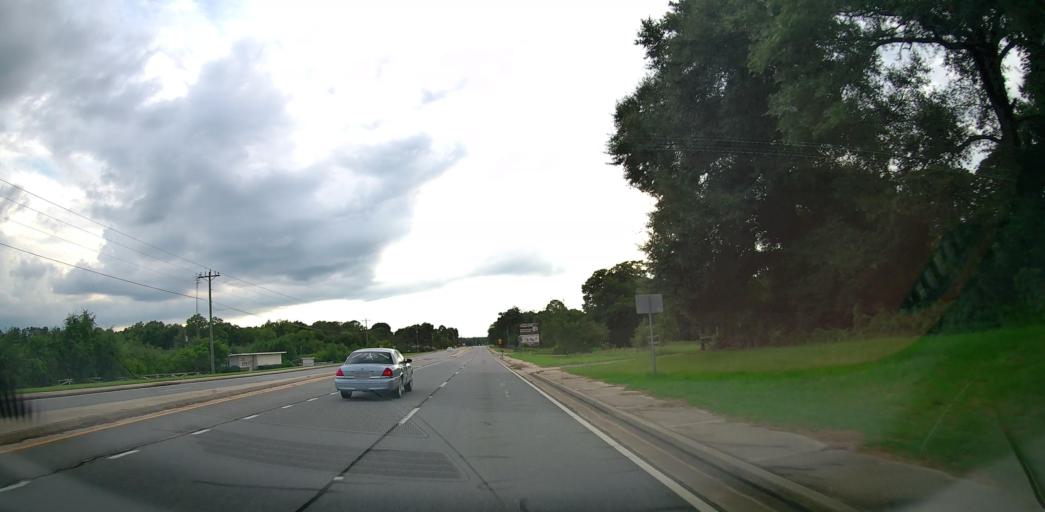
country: US
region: Georgia
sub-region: Pulaski County
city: Hawkinsville
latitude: 32.2818
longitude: -83.4405
